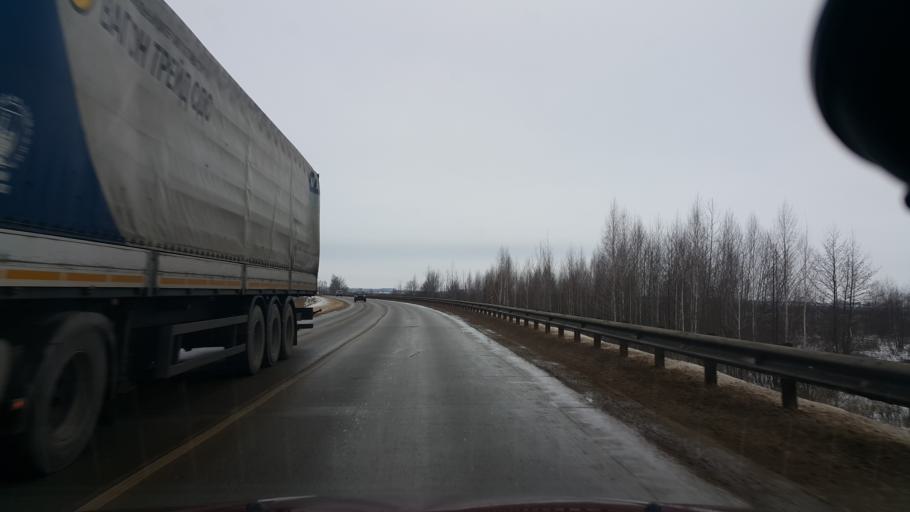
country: RU
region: Tambov
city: Bokino
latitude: 52.6291
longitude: 41.4950
